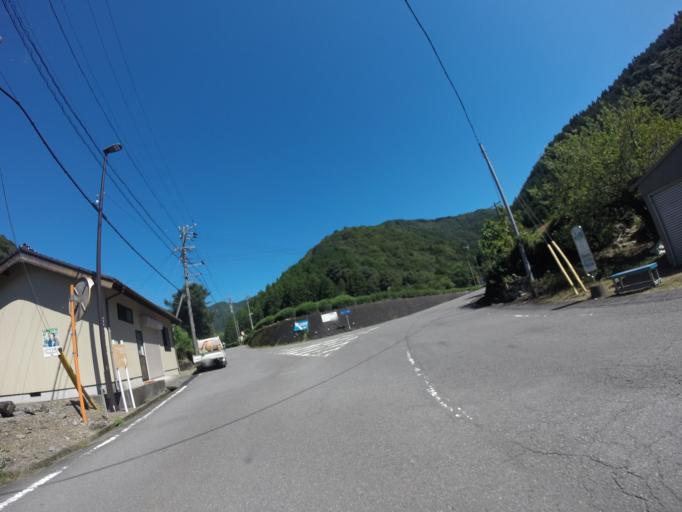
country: JP
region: Shizuoka
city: Kanaya
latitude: 34.9518
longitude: 138.1525
